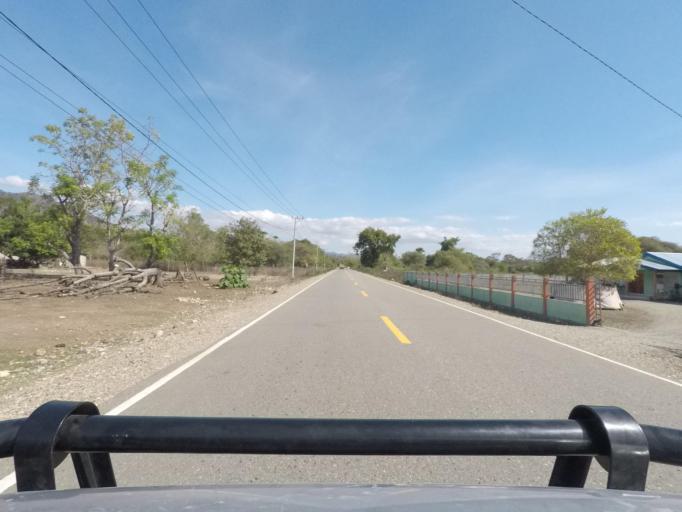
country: ID
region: East Nusa Tenggara
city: Atambua
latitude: -8.9107
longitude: 124.9948
